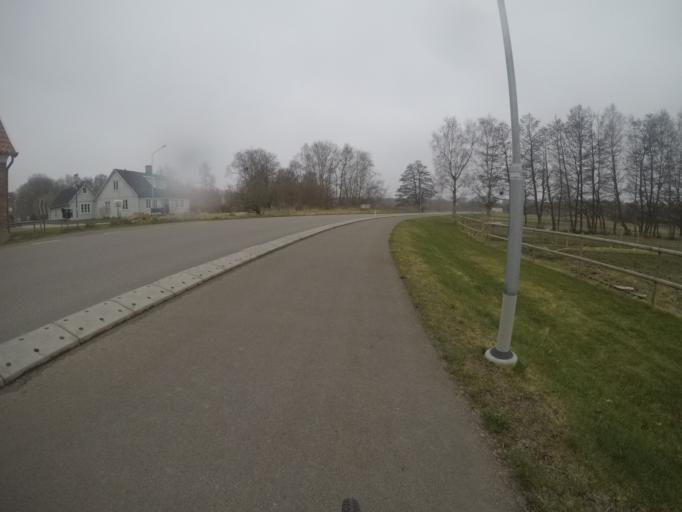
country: SE
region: Skane
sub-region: Angelholms Kommun
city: Vejbystrand
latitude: 56.2157
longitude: 12.7122
